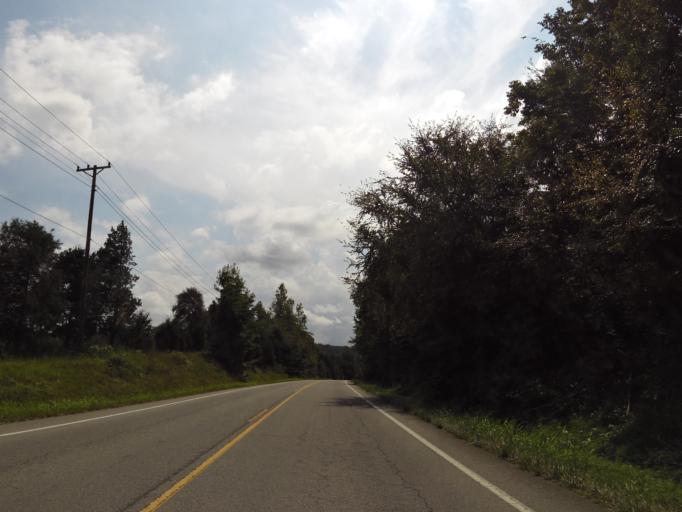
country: US
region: Tennessee
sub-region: Perry County
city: Linden
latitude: 35.8369
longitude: -87.7938
